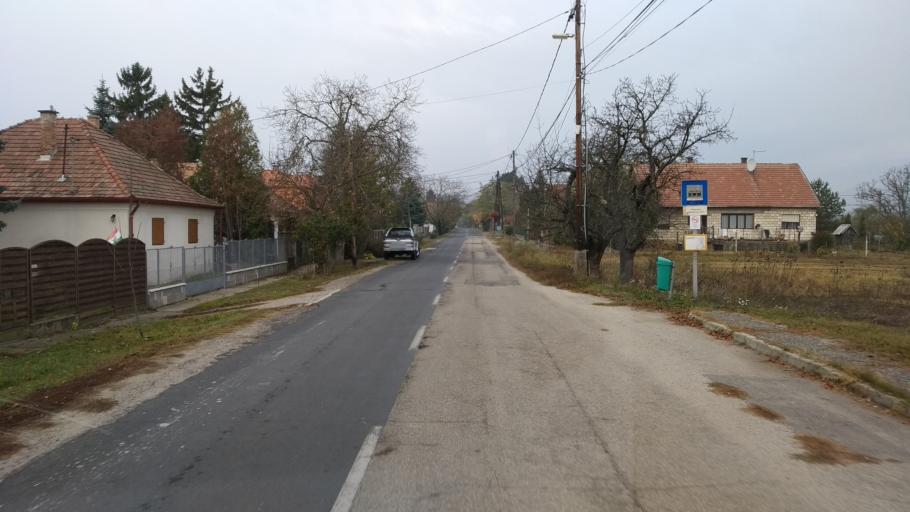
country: HU
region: Pest
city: Veroce
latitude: 47.8054
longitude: 19.0185
